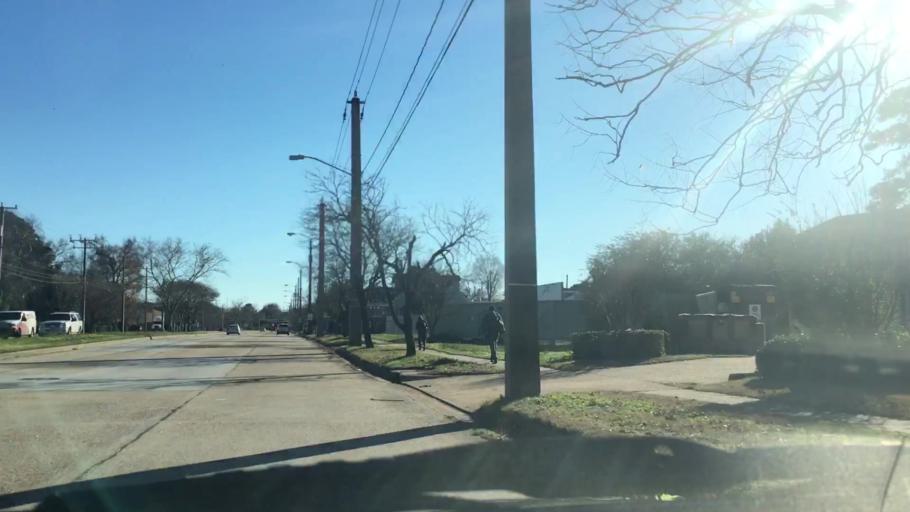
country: US
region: Virginia
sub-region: City of Norfolk
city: Norfolk
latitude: 36.8954
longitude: -76.2385
